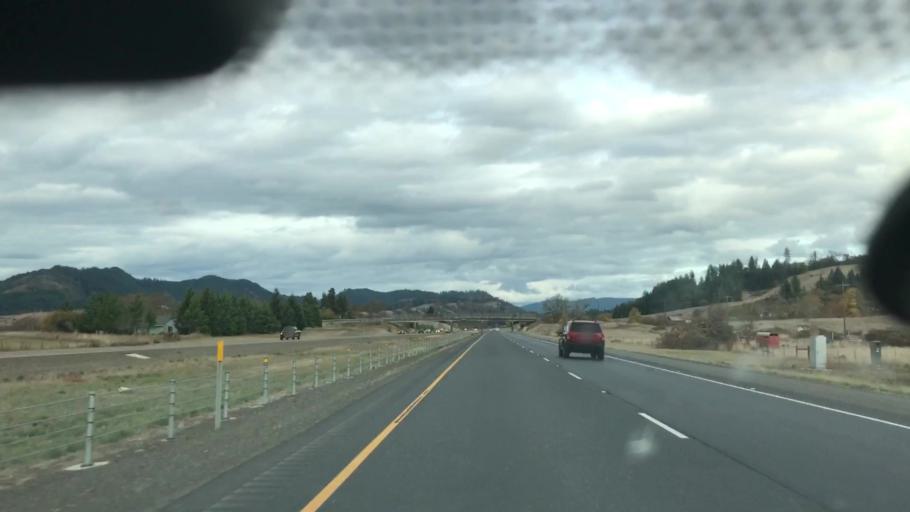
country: US
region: Oregon
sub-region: Douglas County
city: Yoncalla
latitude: 43.5772
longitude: -123.2641
